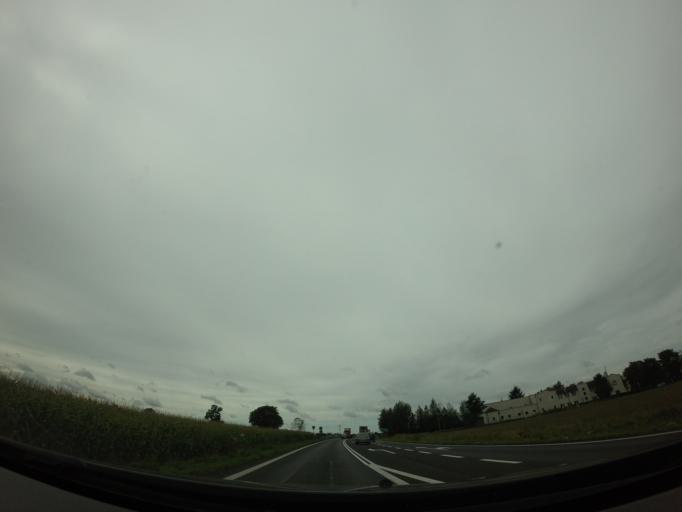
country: PL
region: Greater Poland Voivodeship
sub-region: Powiat szamotulski
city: Pniewy
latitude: 52.4964
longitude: 16.3276
